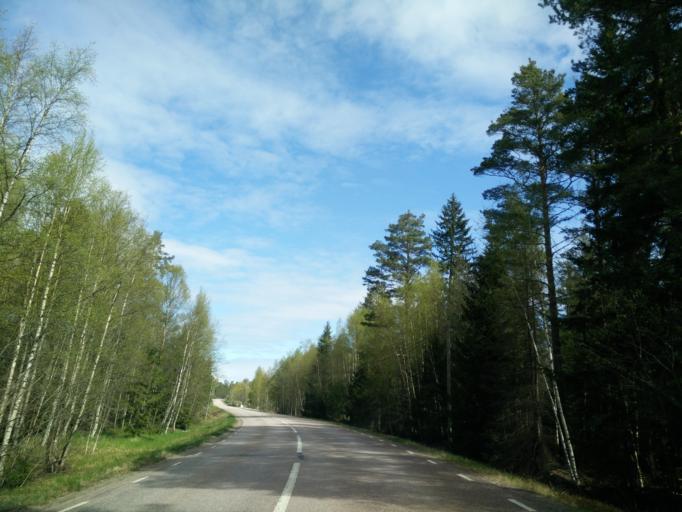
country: SE
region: Gaevleborg
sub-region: Hudiksvalls Kommun
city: Hudiksvall
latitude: 61.8612
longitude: 17.3116
